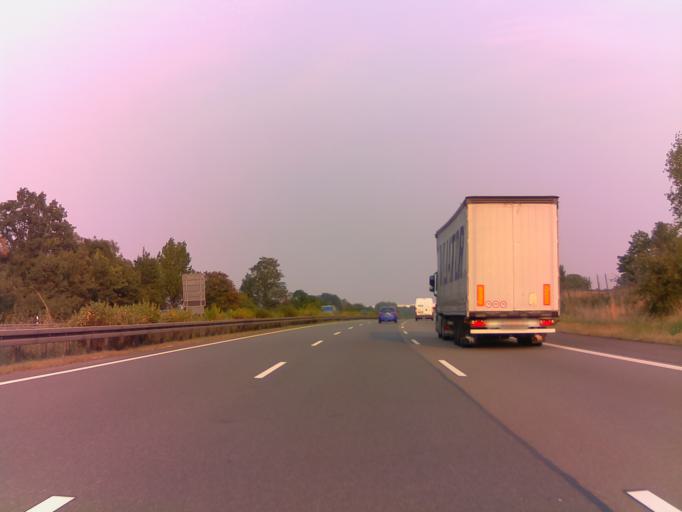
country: DE
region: Thuringia
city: Emleben
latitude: 50.9074
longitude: 10.6614
